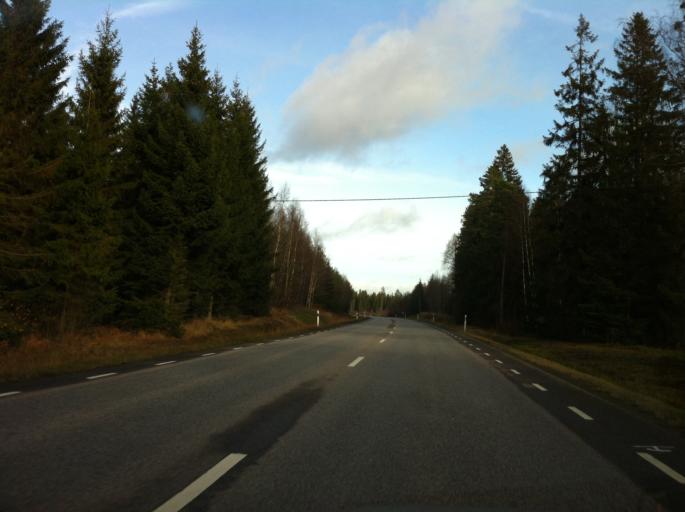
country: SE
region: Kronoberg
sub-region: Almhults Kommun
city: AElmhult
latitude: 56.5986
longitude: 14.2140
